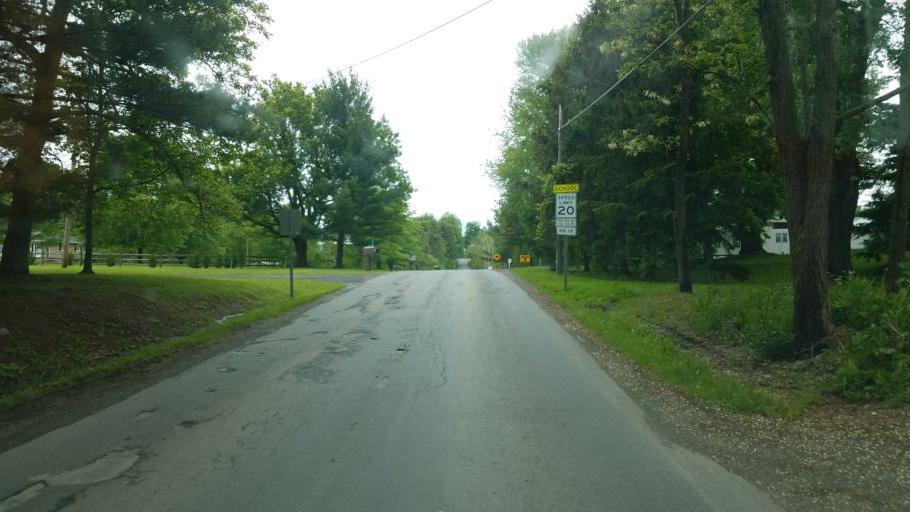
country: US
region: Ohio
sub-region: Geauga County
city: Middlefield
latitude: 41.4020
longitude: -80.9737
